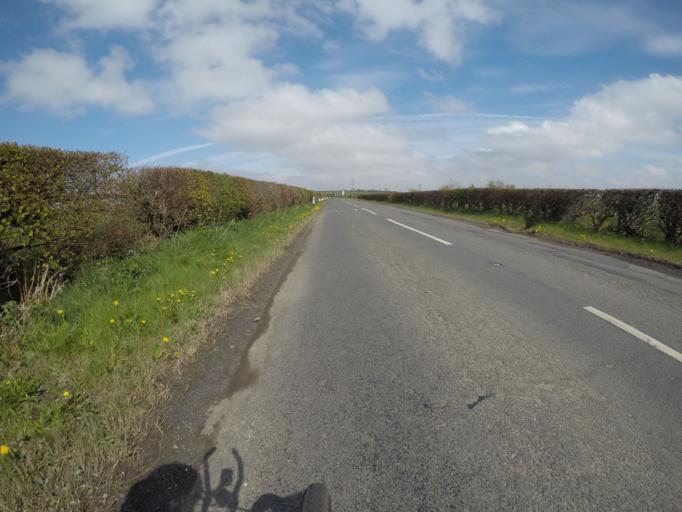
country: GB
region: Scotland
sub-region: East Ayrshire
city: Stewarton
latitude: 55.7007
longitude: -4.4822
